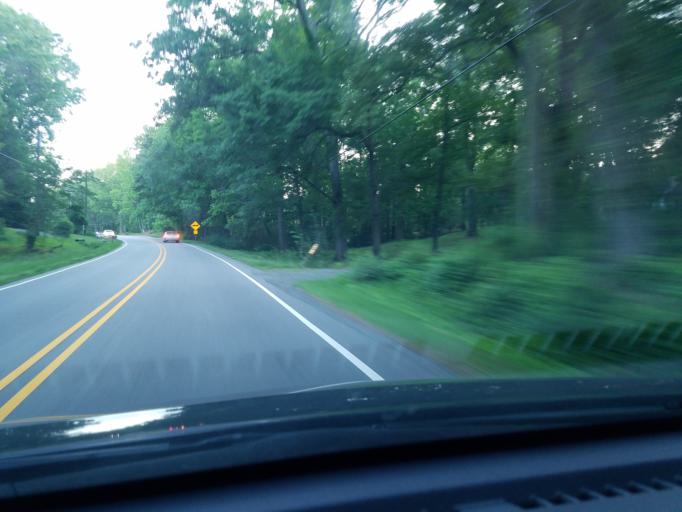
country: US
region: North Carolina
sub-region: Durham County
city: Durham
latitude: 35.9343
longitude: -78.9496
